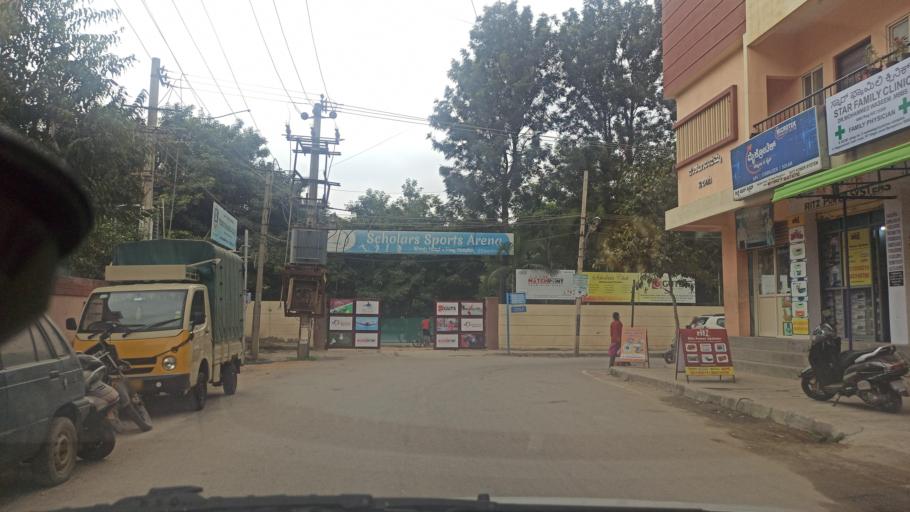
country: IN
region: Karnataka
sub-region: Bangalore Urban
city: Yelahanka
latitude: 13.0376
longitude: 77.6051
